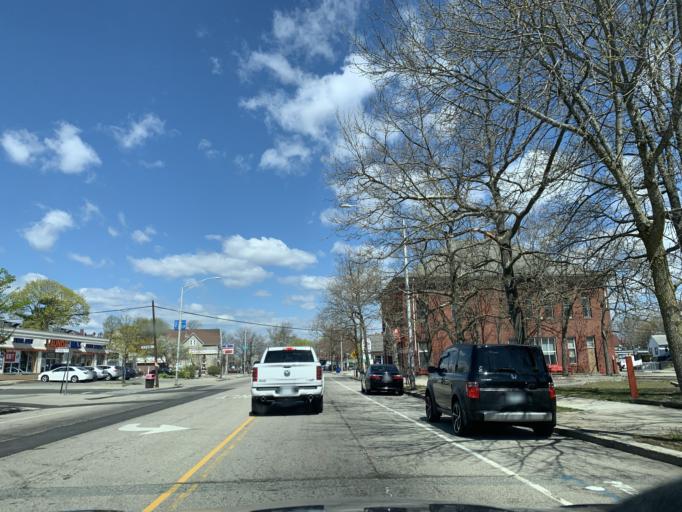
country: US
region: Rhode Island
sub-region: Providence County
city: Cranston
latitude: 41.7904
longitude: -71.4053
